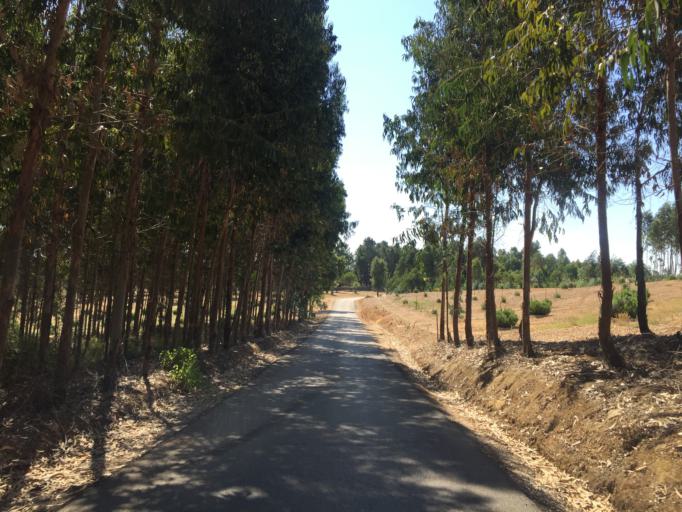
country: PT
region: Santarem
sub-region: Ferreira do Zezere
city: Ferreira do Zezere
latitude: 39.5919
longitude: -8.2854
